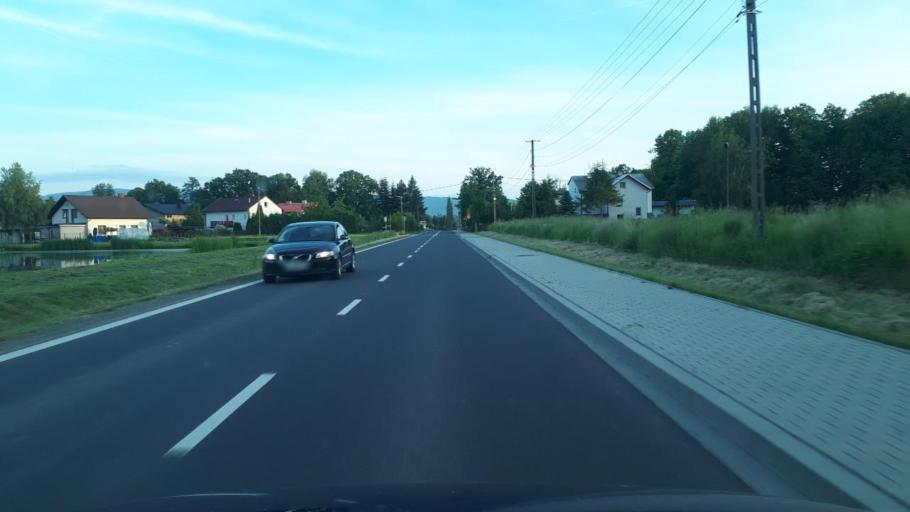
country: PL
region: Silesian Voivodeship
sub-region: Powiat bielski
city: Bronow
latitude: 49.8622
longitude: 18.9453
